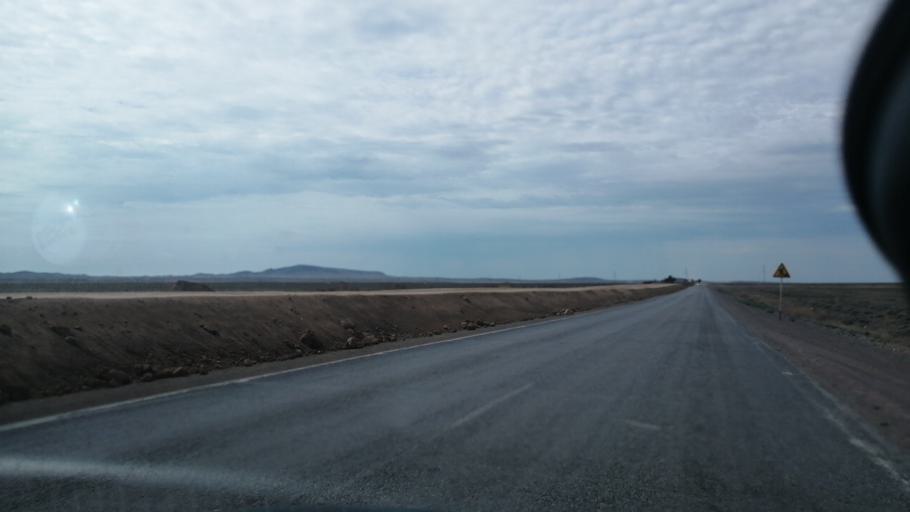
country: KZ
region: Qaraghandy
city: Balqash
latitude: 46.6903
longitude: 74.4357
